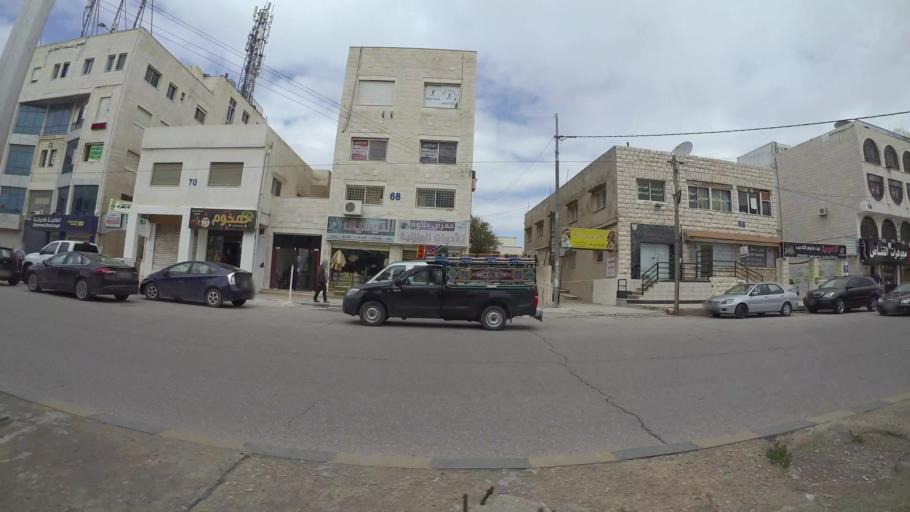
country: JO
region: Amman
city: Wadi as Sir
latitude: 31.9541
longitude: 35.8377
